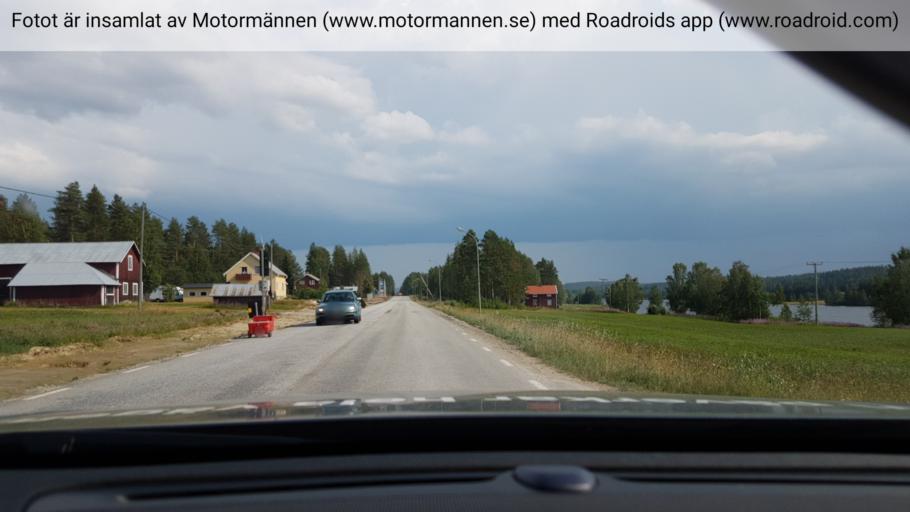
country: SE
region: Vaesterbotten
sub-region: Bjurholms Kommun
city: Bjurholm
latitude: 64.2187
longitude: 19.3811
